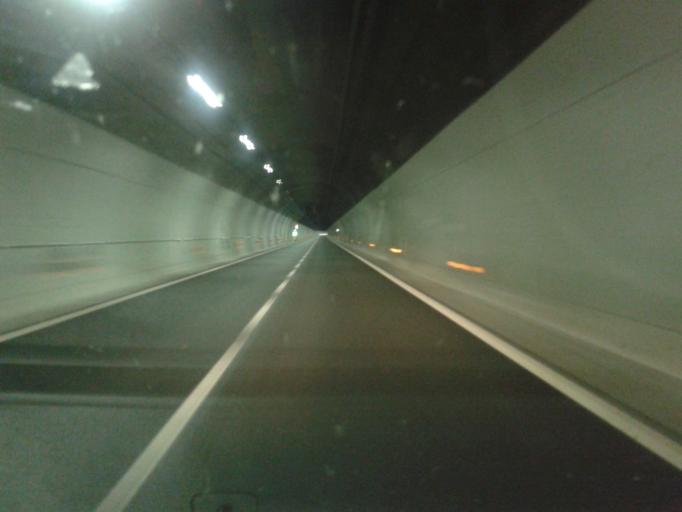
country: IT
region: Friuli Venezia Giulia
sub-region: Provincia di Udine
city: Dogna
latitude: 46.4718
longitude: 13.2984
